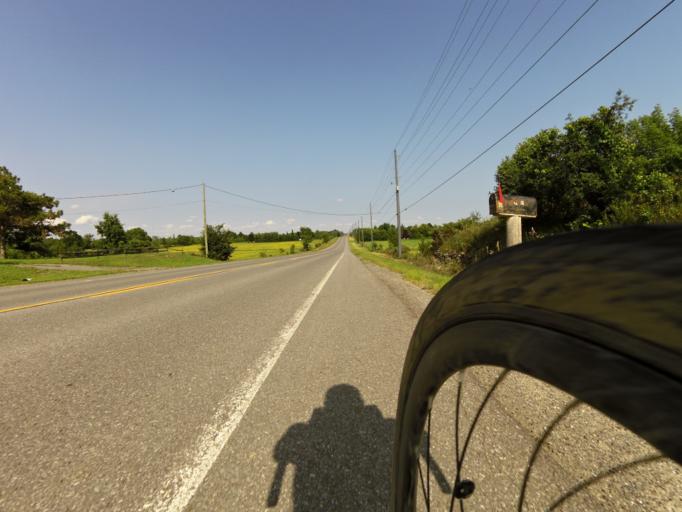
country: CA
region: Ontario
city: Kingston
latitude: 44.3029
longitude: -76.6926
